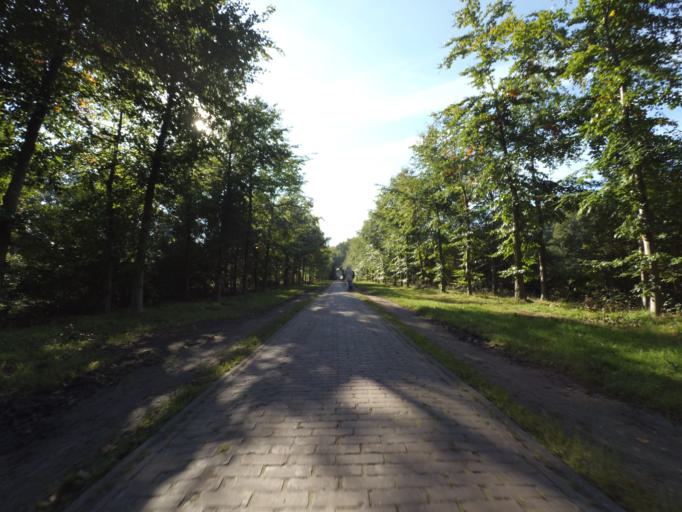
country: NL
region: Utrecht
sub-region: Gemeente Leusden
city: Leusden
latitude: 52.1811
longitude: 5.4437
